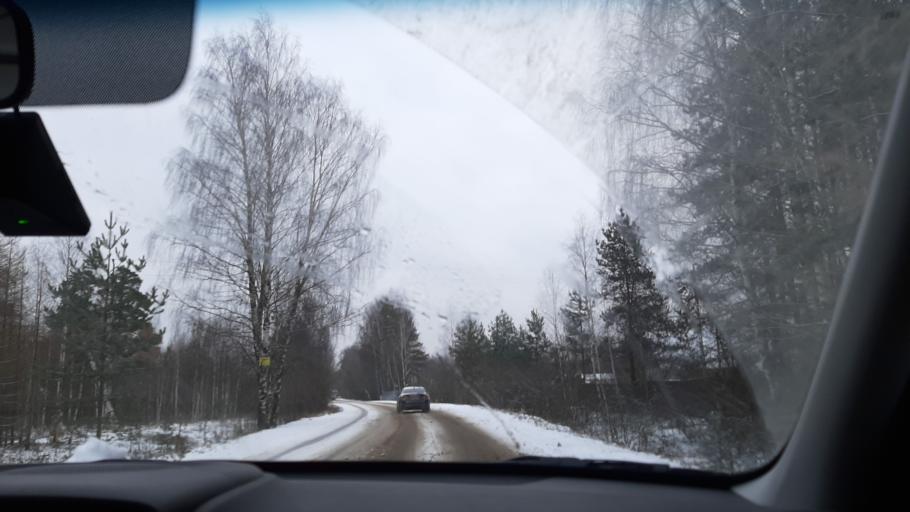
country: RU
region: Ivanovo
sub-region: Gorod Ivanovo
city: Ivanovo
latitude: 56.9340
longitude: 40.9696
